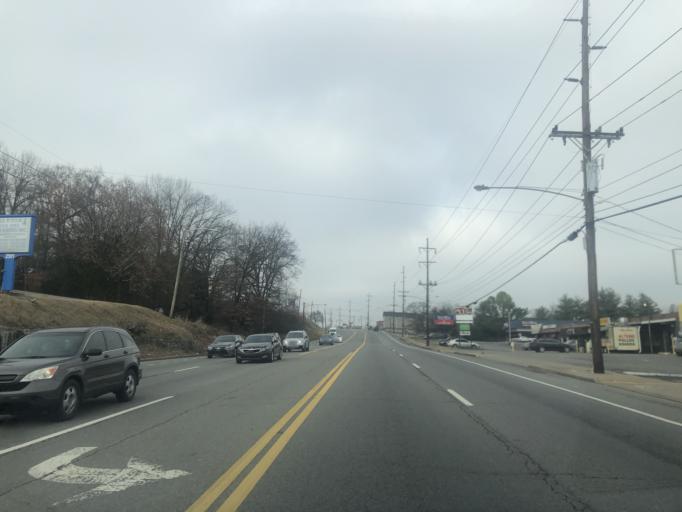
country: US
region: Tennessee
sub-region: Rutherford County
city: La Vergne
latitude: 36.0747
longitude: -86.6388
